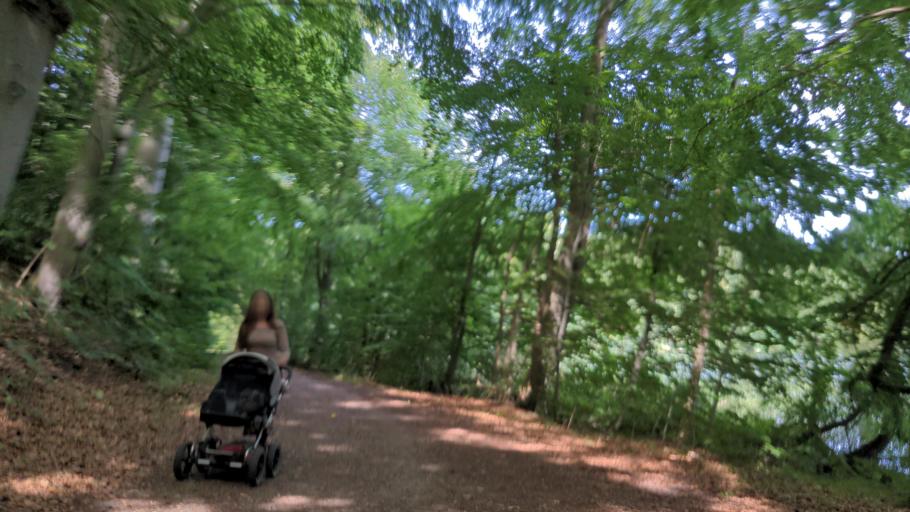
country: DE
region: Schleswig-Holstein
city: Eutin
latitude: 54.1820
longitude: 10.6293
